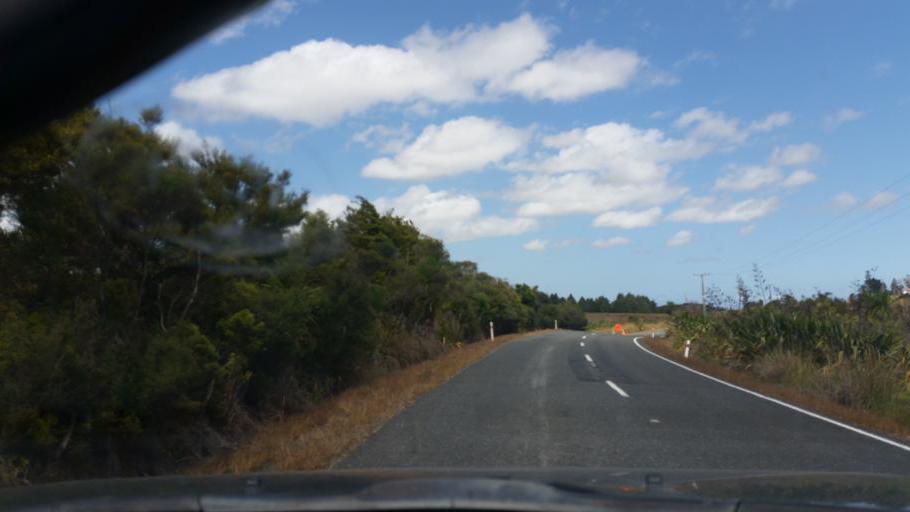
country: NZ
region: Northland
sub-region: Kaipara District
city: Dargaville
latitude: -35.8756
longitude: 173.8461
